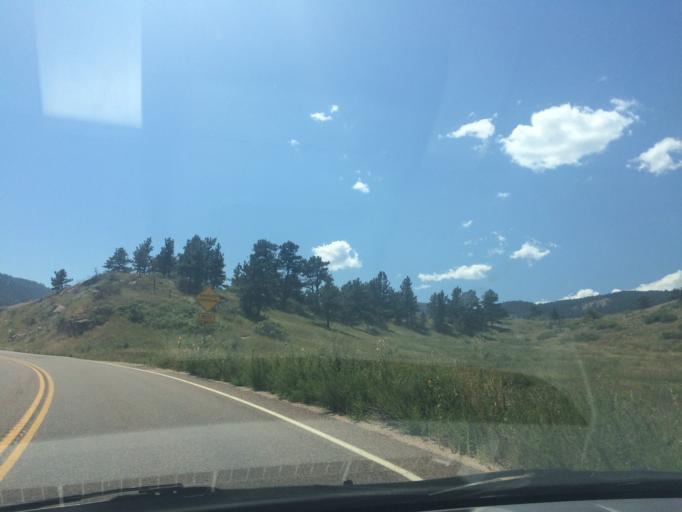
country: US
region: Colorado
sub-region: Boulder County
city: Lyons
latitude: 40.2053
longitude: -105.2999
